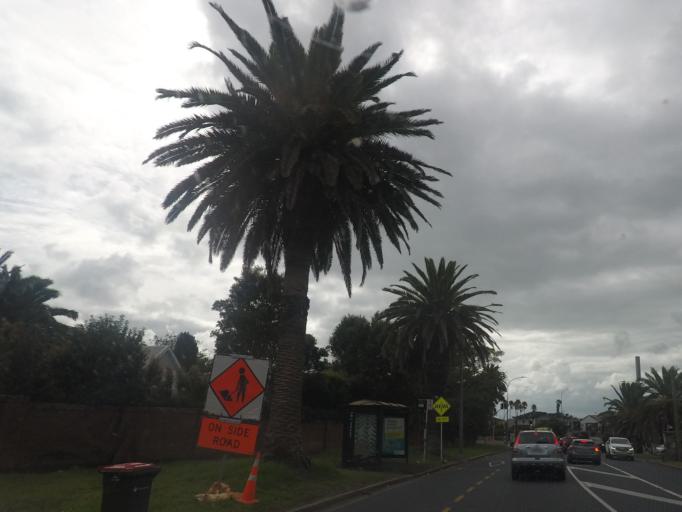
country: NZ
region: Auckland
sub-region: Auckland
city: Tamaki
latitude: -36.8599
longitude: 174.8360
